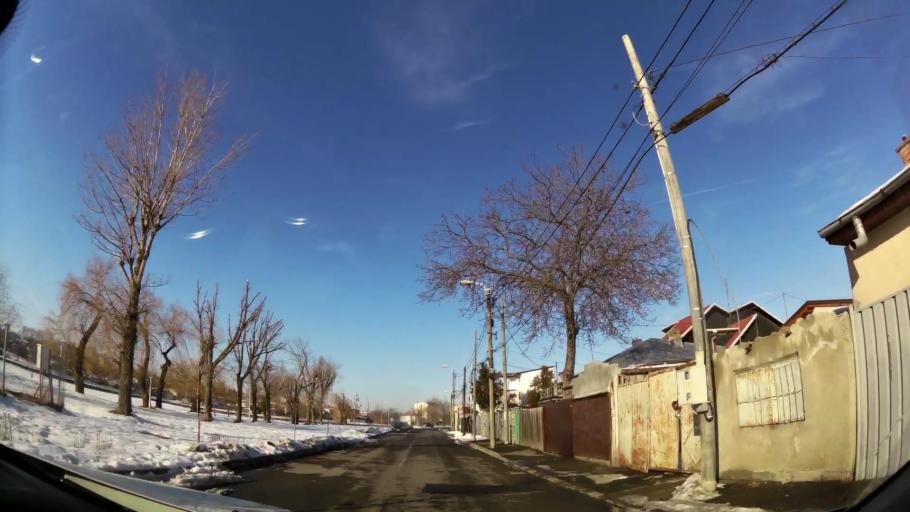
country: RO
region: Ilfov
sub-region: Comuna Fundeni-Dobroesti
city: Fundeni
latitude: 44.4682
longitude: 26.1312
